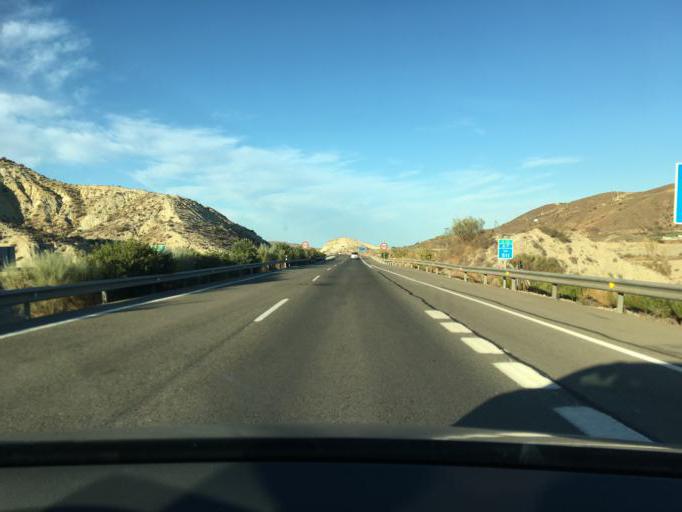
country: ES
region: Andalusia
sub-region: Provincia de Almeria
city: Sorbas
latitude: 37.1092
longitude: -2.0293
